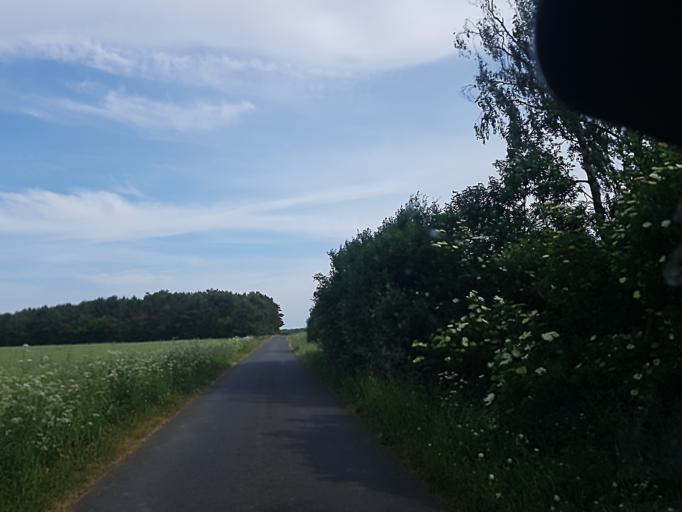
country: DE
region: Brandenburg
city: Niemegk
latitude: 52.0062
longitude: 12.6662
